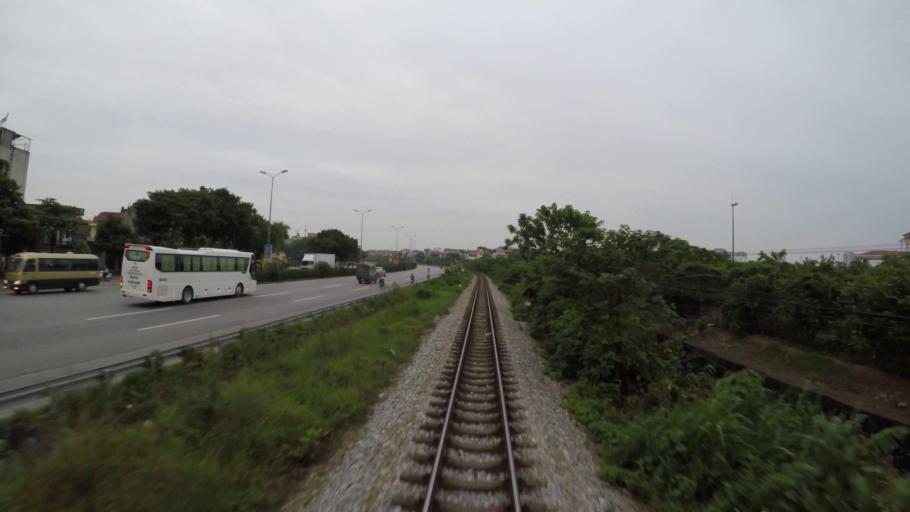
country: VN
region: Ha Noi
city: Trau Quy
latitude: 21.0095
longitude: 105.9541
